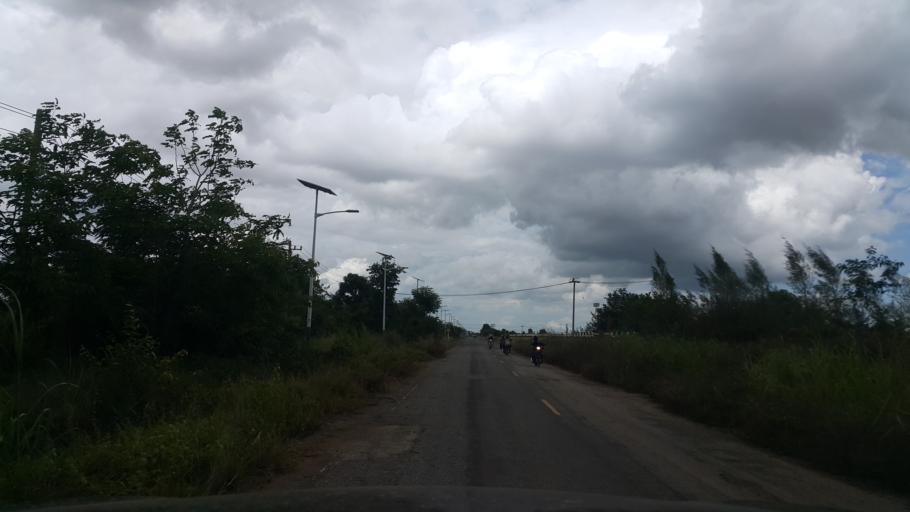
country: TH
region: Sukhothai
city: Sukhothai
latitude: 17.0623
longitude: 99.7884
